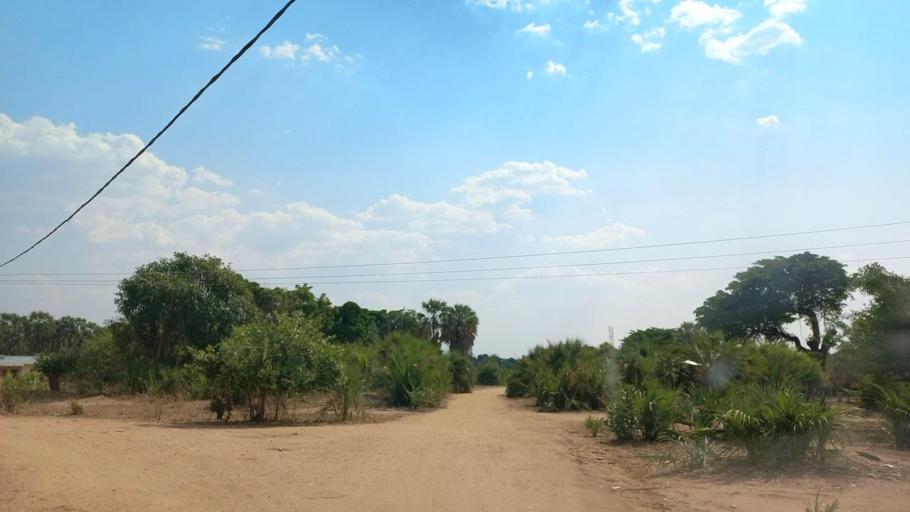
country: ZM
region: Lusaka
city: Luangwa
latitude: -15.0865
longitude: 30.1904
